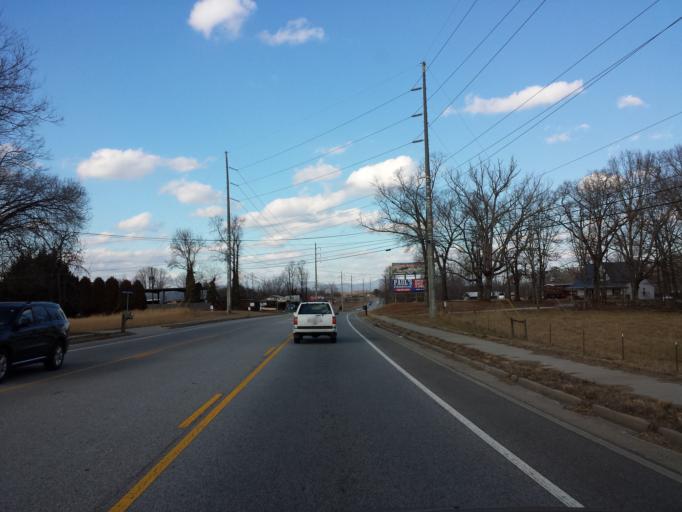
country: US
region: Georgia
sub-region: White County
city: Cleveland
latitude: 34.6206
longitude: -83.7541
